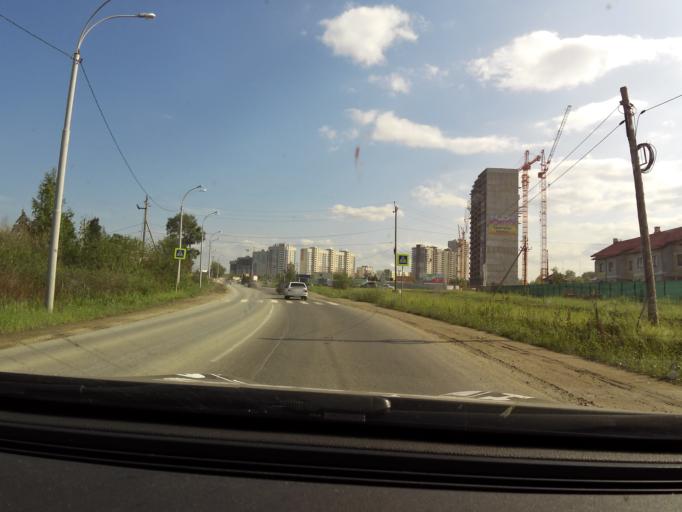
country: RU
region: Sverdlovsk
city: Shirokaya Rechka
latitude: 56.8015
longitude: 60.4940
